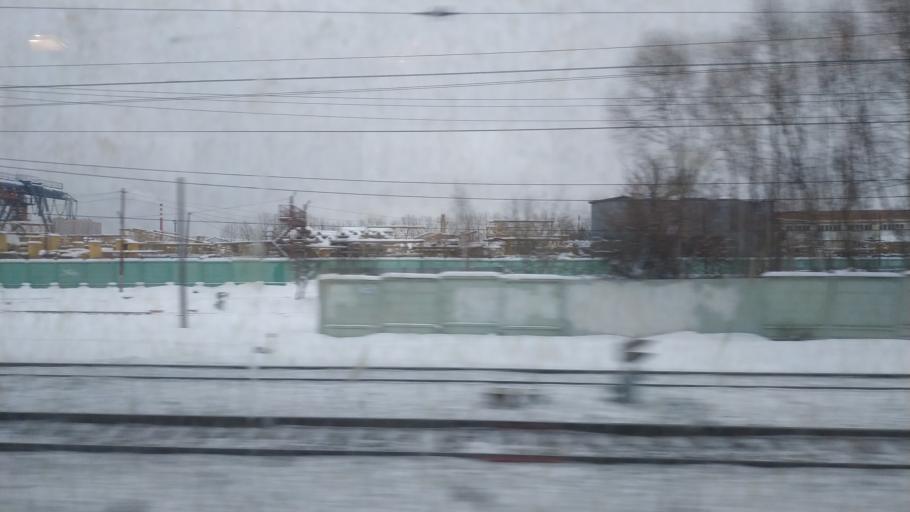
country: RU
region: Moskovskaya
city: Shcherbinka
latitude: 55.4749
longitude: 37.5550
